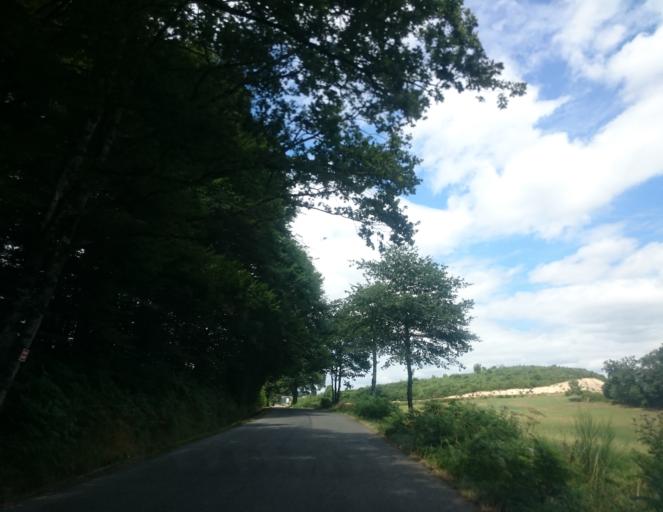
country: FR
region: Auvergne
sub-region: Departement du Cantal
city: Laroquebrou
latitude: 44.9307
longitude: 2.1937
